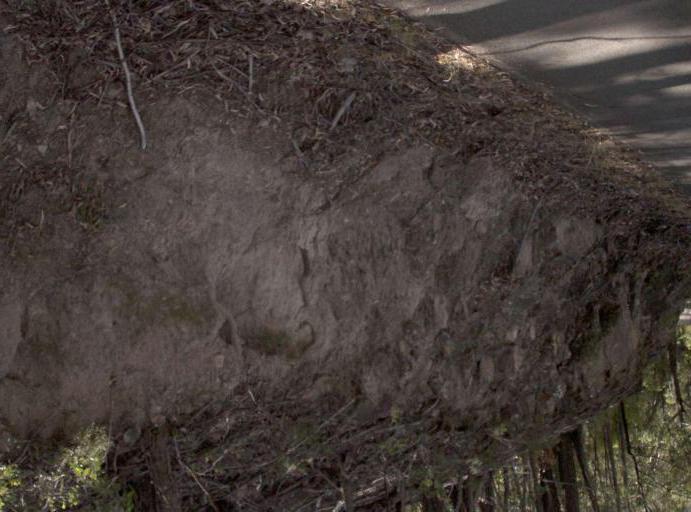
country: AU
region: Victoria
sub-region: East Gippsland
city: Lakes Entrance
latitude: -37.3947
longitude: 148.1224
